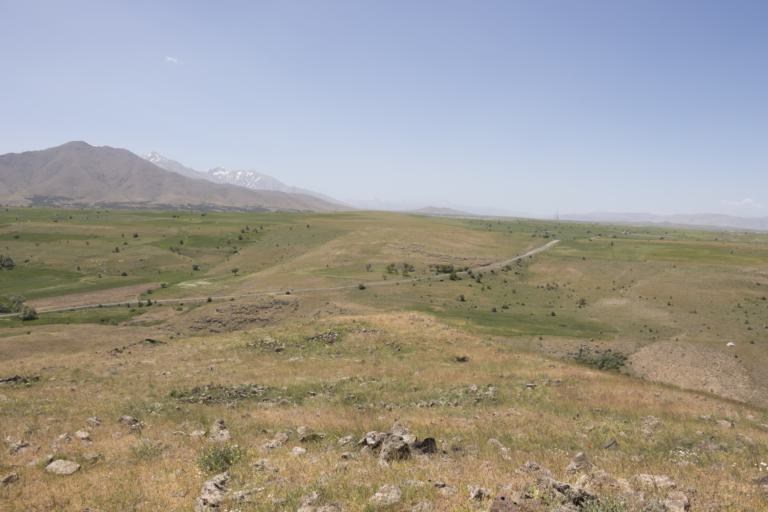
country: TR
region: Kayseri
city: Toklar
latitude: 38.4427
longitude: 36.0499
